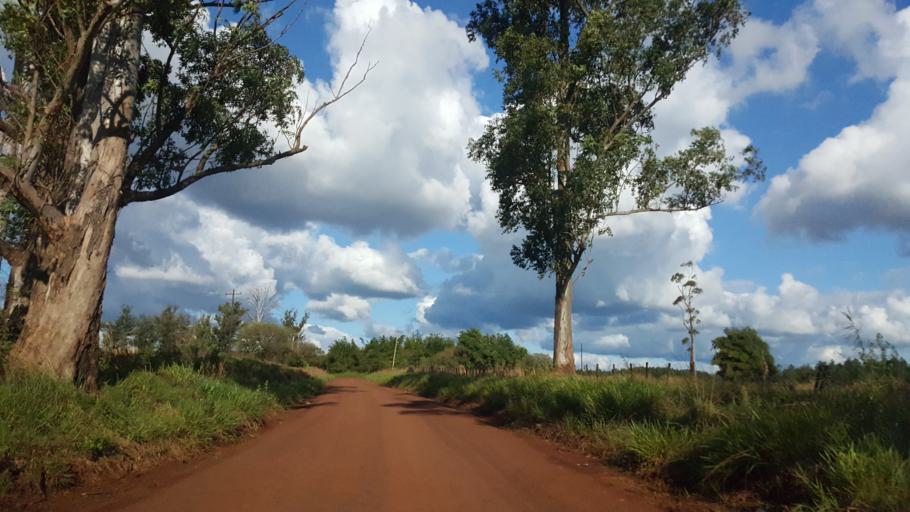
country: AR
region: Misiones
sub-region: Departamento de Capital
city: Posadas
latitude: -27.4210
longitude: -55.9990
